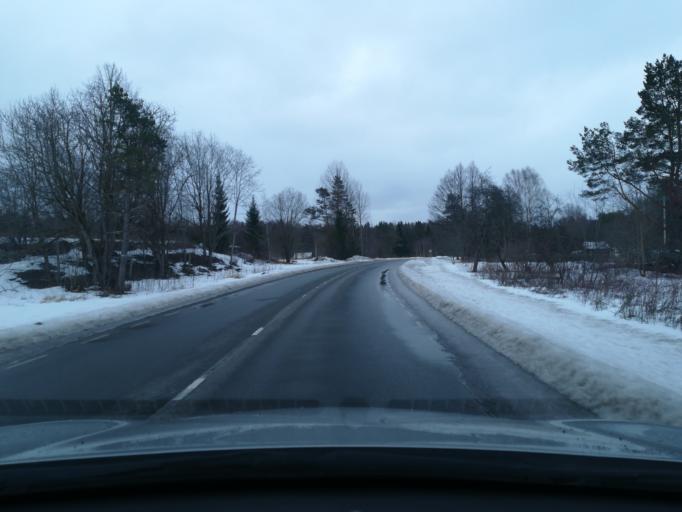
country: EE
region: Harju
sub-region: Nissi vald
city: Turba
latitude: 59.0730
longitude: 24.2469
